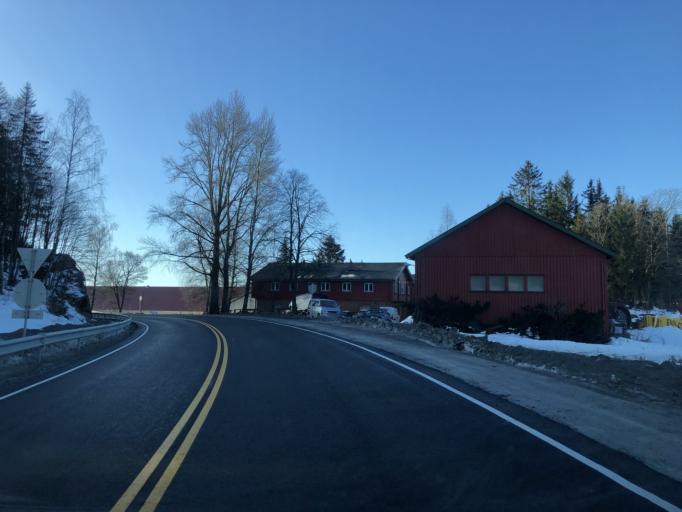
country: NO
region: Hedmark
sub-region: Ringsaker
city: Moelv
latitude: 60.9101
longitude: 10.7056
